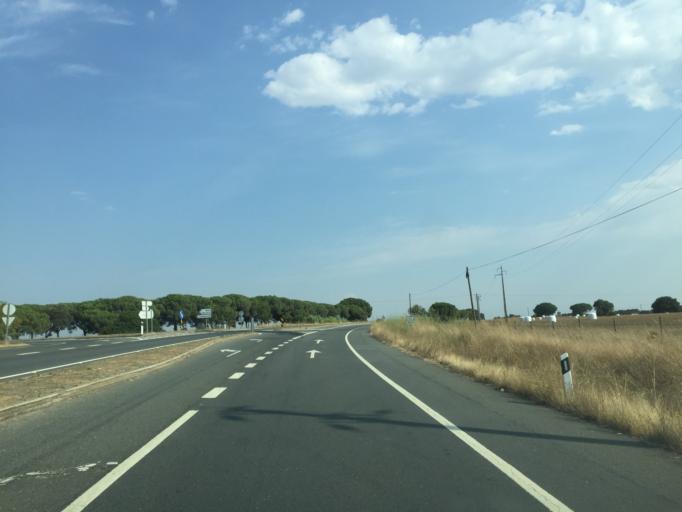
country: PT
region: Setubal
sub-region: Grandola
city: Grandola
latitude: 38.0097
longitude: -8.3793
